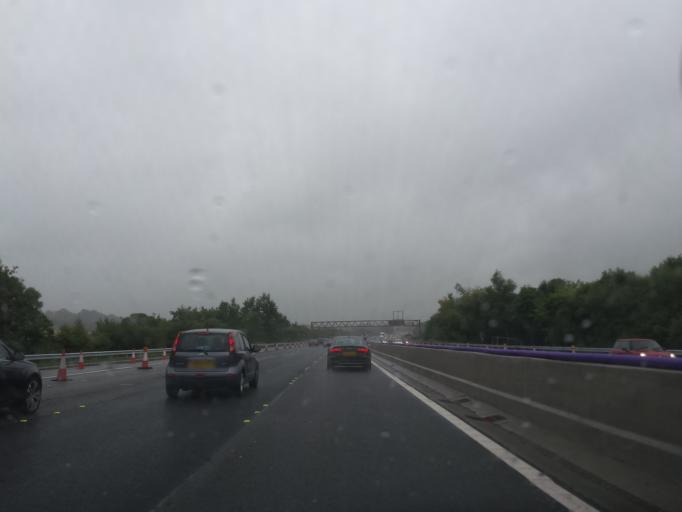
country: GB
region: England
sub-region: Derbyshire
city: Tibshelf
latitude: 53.1847
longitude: -1.3230
